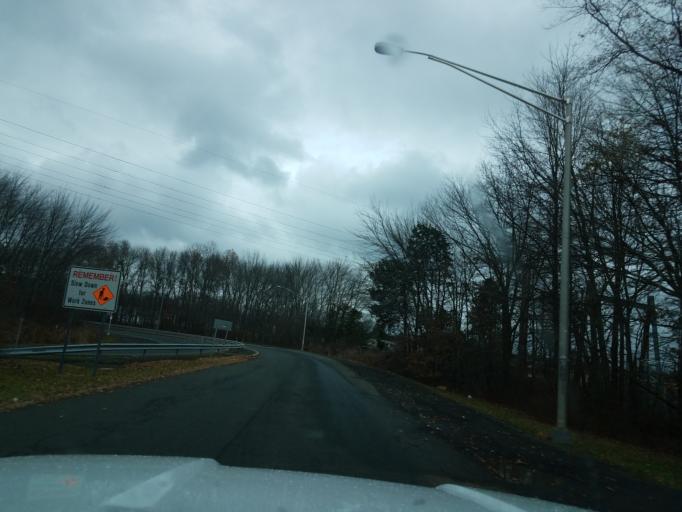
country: US
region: Connecticut
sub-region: New Haven County
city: Cheshire Village
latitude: 41.5732
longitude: -72.9032
